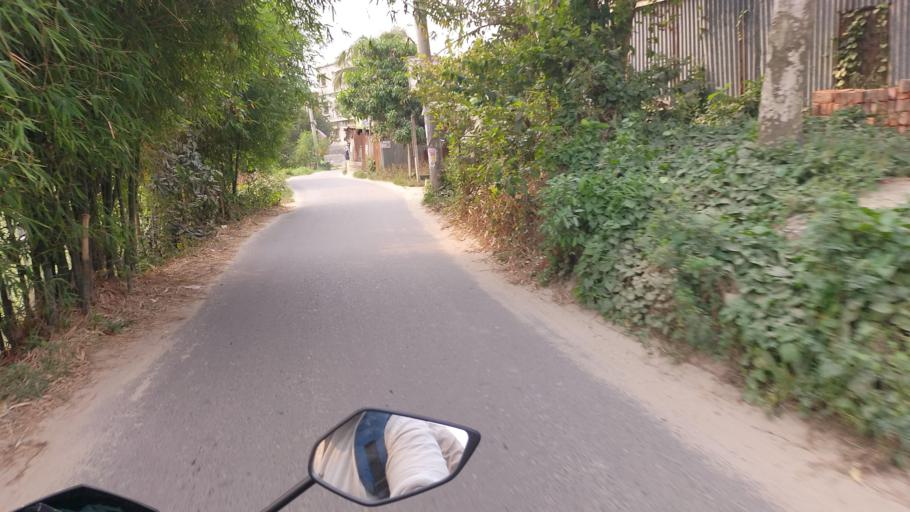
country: BD
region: Dhaka
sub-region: Dhaka
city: Dhaka
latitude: 23.6644
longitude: 90.3529
